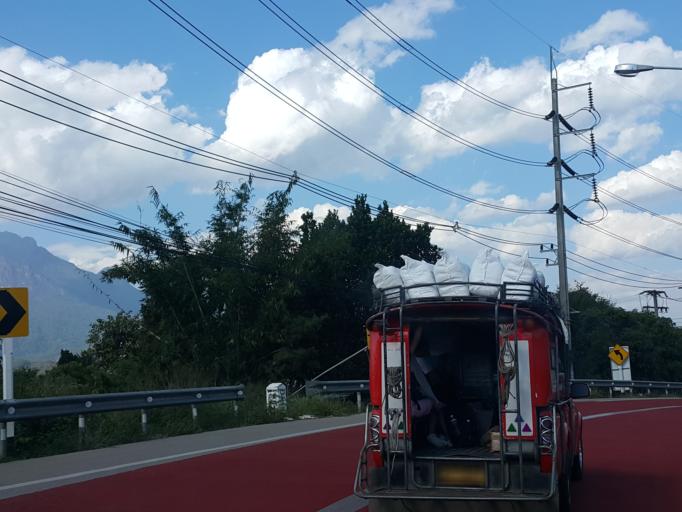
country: TH
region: Chiang Mai
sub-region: Amphoe Chiang Dao
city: Chiang Dao
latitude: 19.3231
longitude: 98.9534
